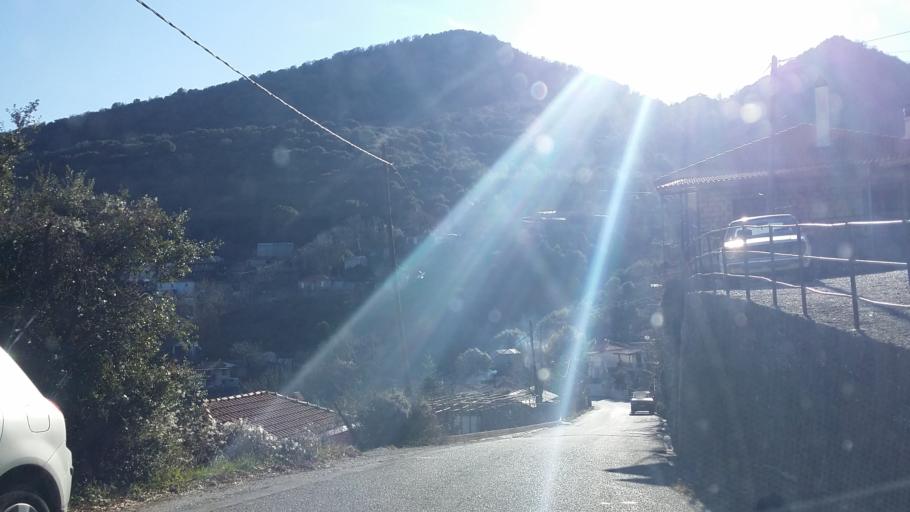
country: GR
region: Central Greece
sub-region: Nomos Evrytanias
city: Kerasochori
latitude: 38.9587
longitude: 21.6007
